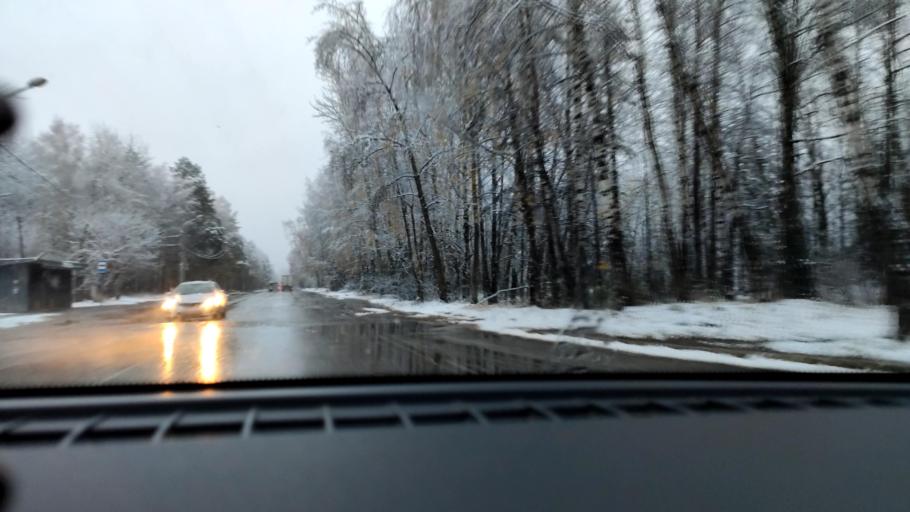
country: RU
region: Perm
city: Overyata
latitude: 58.0145
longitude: 55.9066
